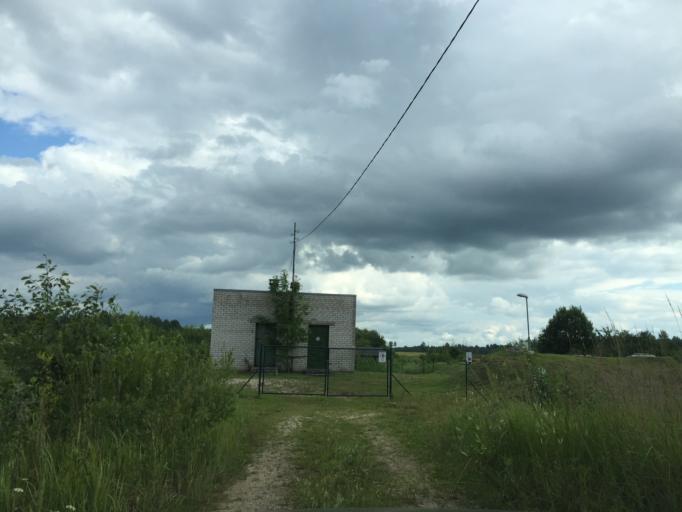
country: LV
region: Malpils
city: Malpils
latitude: 56.8552
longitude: 25.0164
